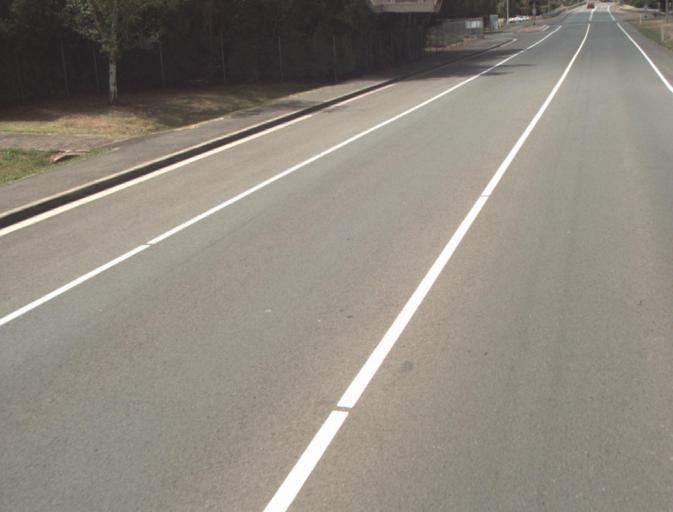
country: AU
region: Tasmania
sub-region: Launceston
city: Newstead
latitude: -41.4387
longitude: 147.1682
